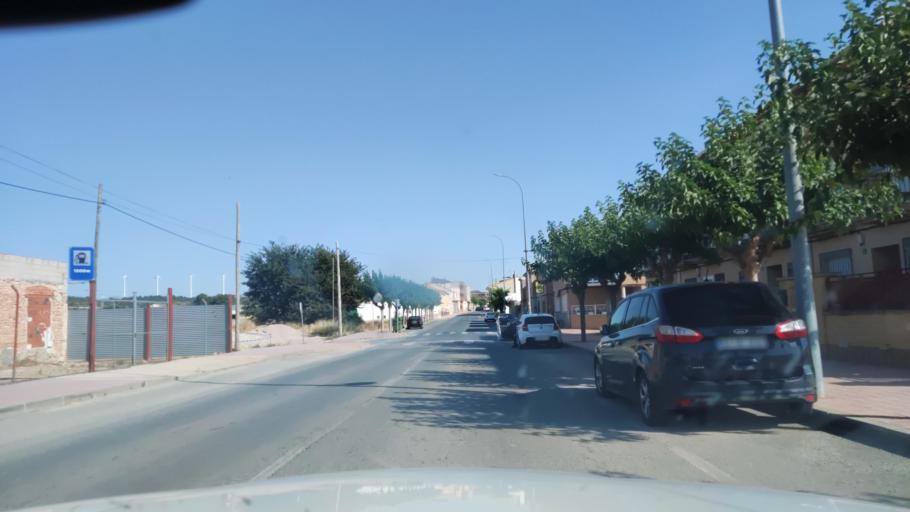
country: ES
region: Castille-La Mancha
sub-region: Provincia de Albacete
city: Pozo-Canada
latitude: 38.8068
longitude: -1.7351
